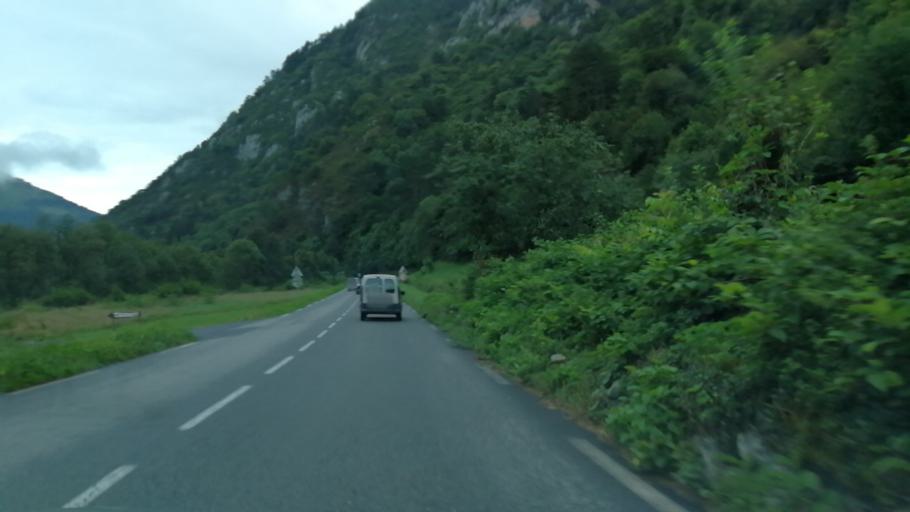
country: FR
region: Aquitaine
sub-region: Departement des Pyrenees-Atlantiques
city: Arette
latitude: 43.0207
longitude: -0.6023
